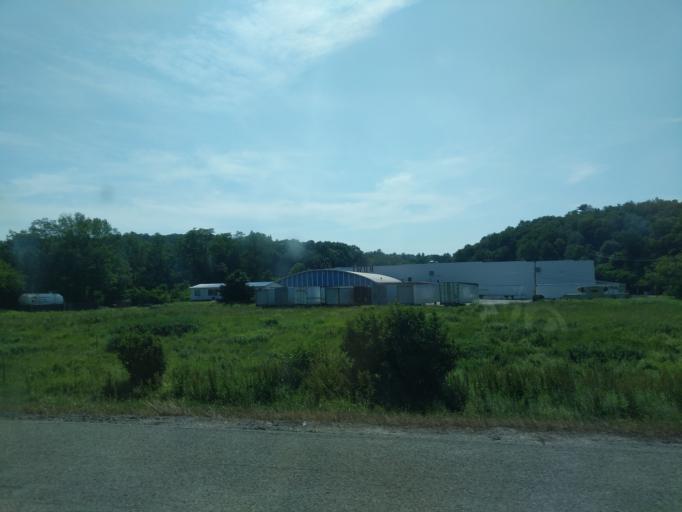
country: US
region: New York
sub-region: Sullivan County
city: Liberty
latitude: 41.7979
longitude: -74.7353
